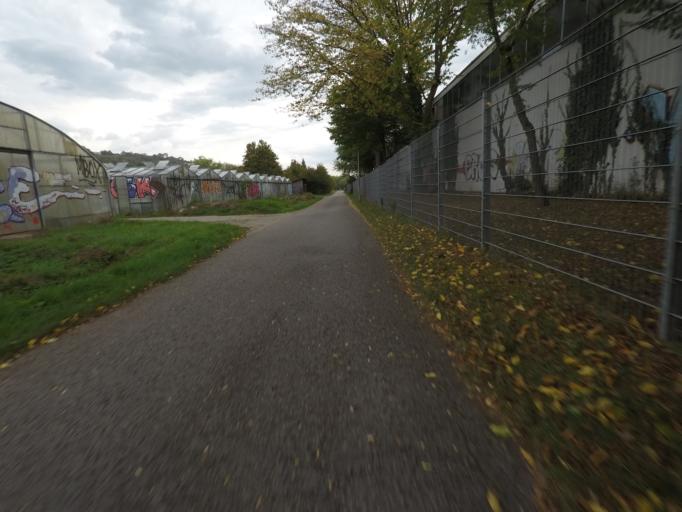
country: DE
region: Baden-Wuerttemberg
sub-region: Tuebingen Region
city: Tuebingen
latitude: 48.5217
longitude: 9.0314
